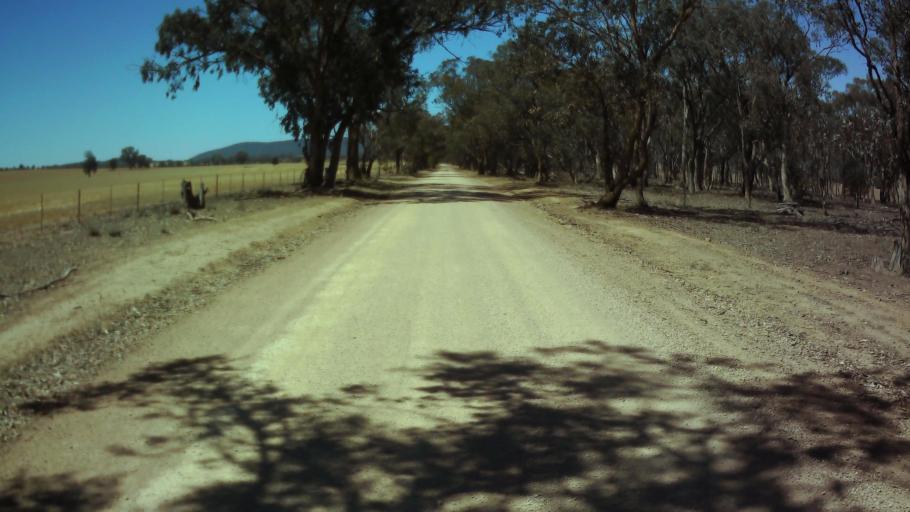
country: AU
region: New South Wales
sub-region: Weddin
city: Grenfell
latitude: -33.9123
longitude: 148.0797
